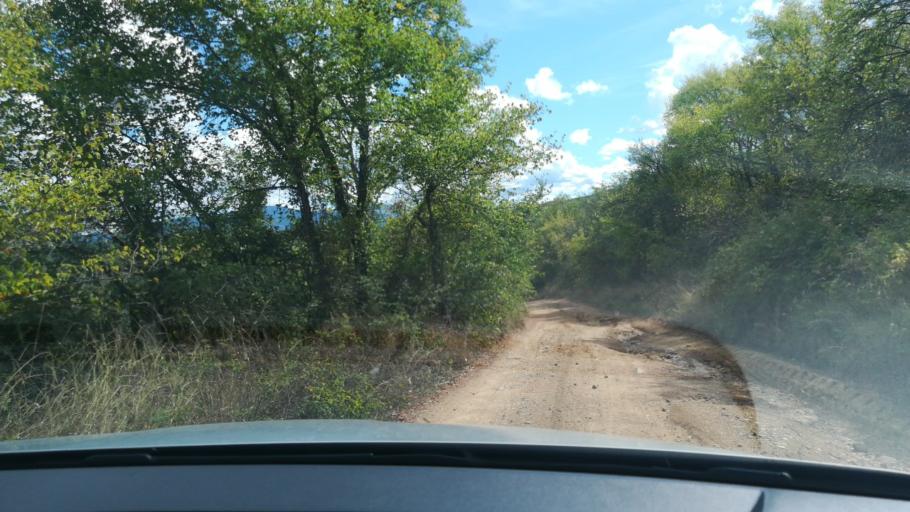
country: MK
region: Delcevo
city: Delcevo
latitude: 41.8902
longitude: 22.8045
